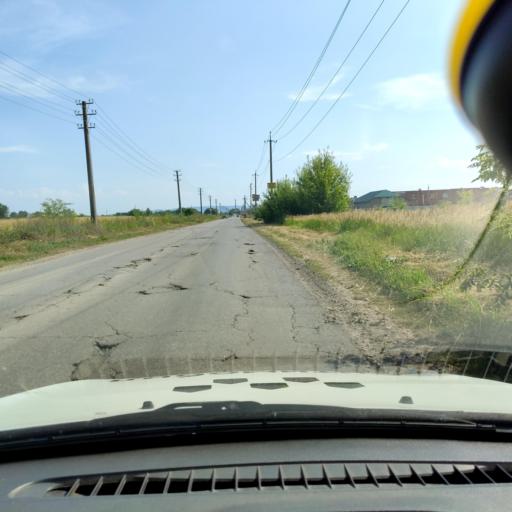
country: RU
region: Samara
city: Podstepki
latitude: 53.5194
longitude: 49.1949
